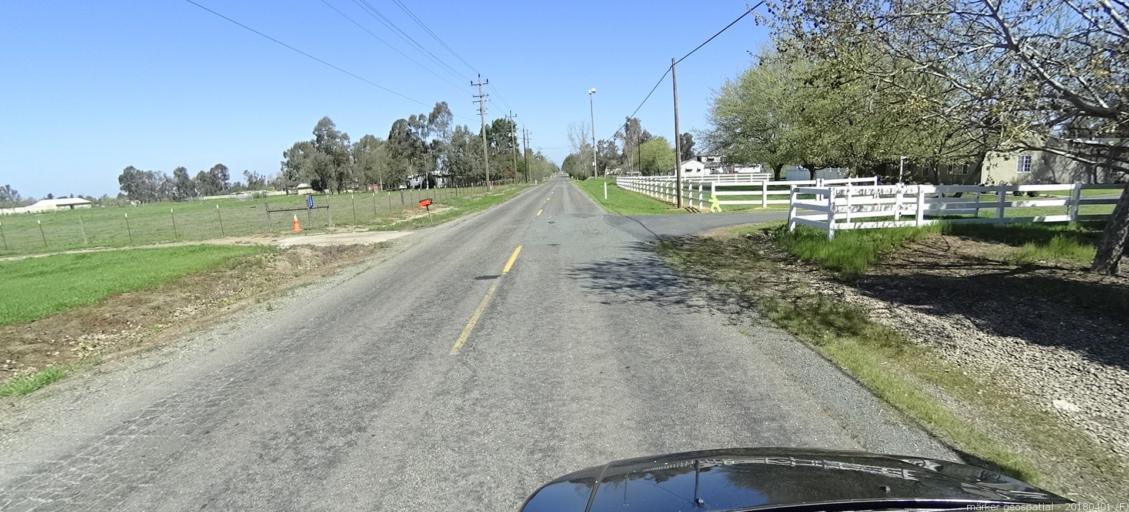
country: US
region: California
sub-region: Sacramento County
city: Herald
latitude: 38.3362
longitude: -121.2421
